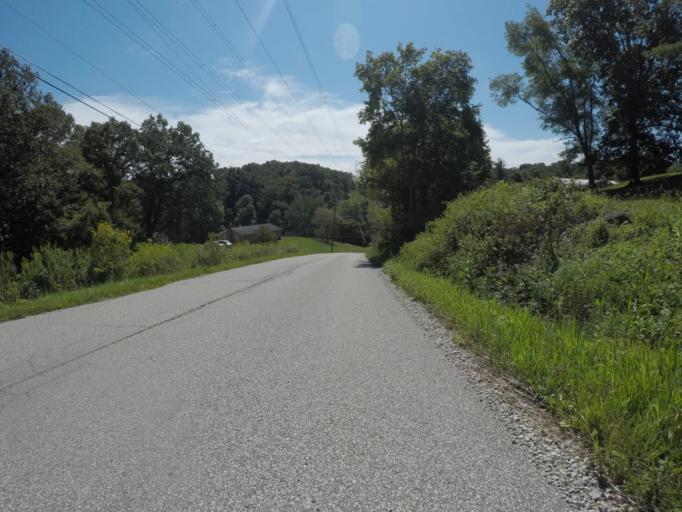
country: US
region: Kentucky
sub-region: Boyd County
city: Catlettsburg
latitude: 38.4034
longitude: -82.6501
